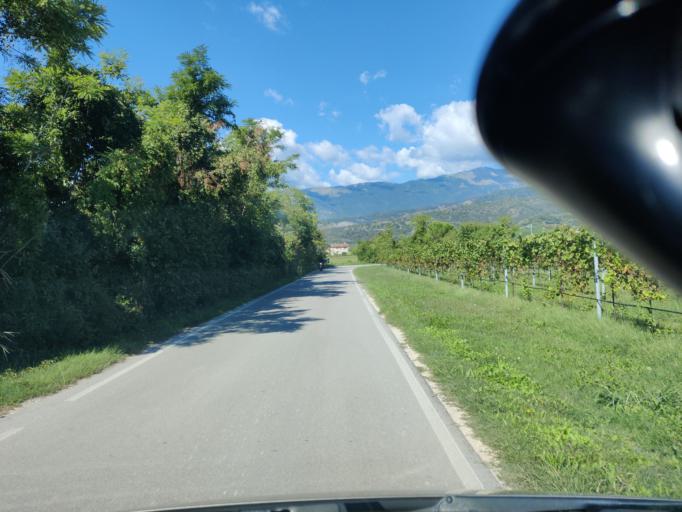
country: IT
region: Veneto
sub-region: Provincia di Treviso
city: Cappella Maggiore
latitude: 45.9746
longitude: 12.3350
